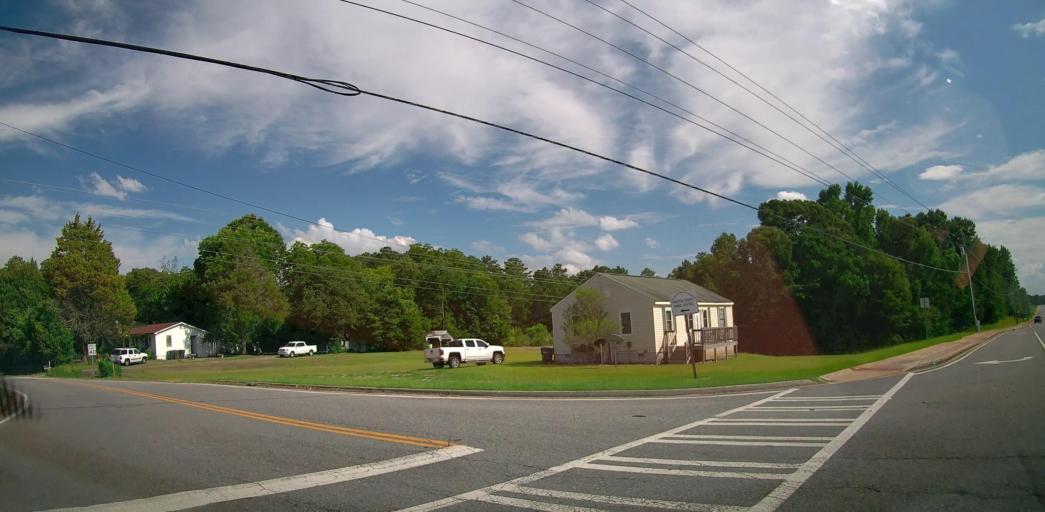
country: US
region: Georgia
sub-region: Houston County
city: Robins Air Force Base
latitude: 32.5278
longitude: -83.6350
